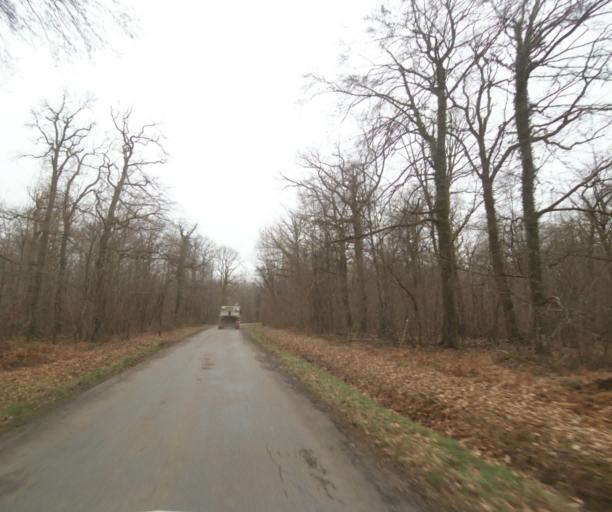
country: FR
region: Champagne-Ardenne
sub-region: Departement de la Haute-Marne
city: Wassy
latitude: 48.5242
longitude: 4.9757
